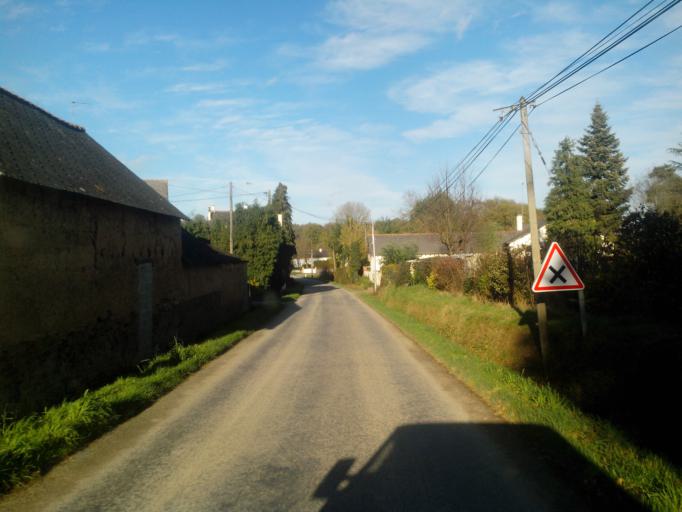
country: FR
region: Brittany
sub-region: Departement du Morbihan
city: Guilliers
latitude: 48.0539
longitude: -2.4011
